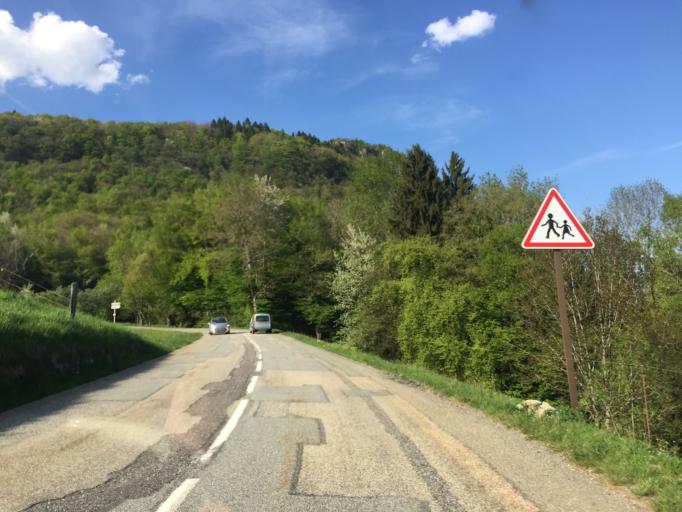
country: FR
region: Rhone-Alpes
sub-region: Departement de la Savoie
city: Frontenex
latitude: 45.6631
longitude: 6.3066
